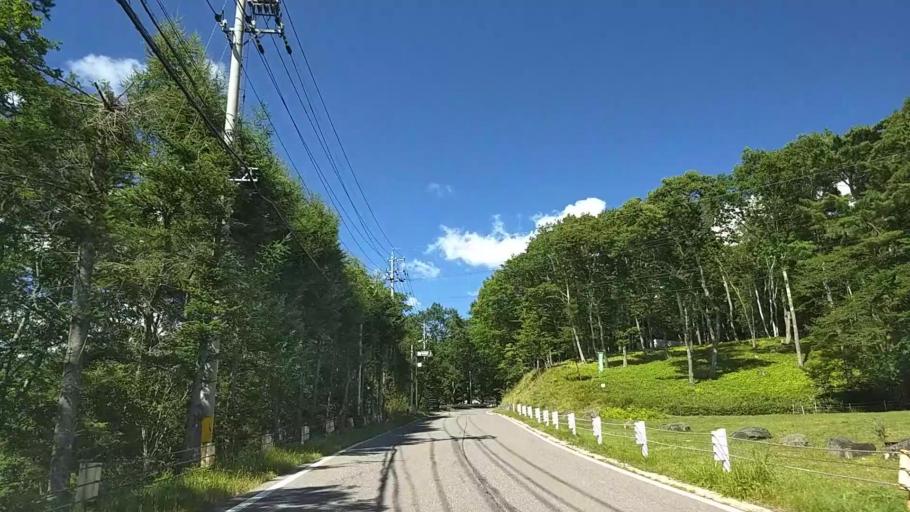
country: JP
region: Nagano
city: Chino
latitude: 36.0650
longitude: 138.2891
